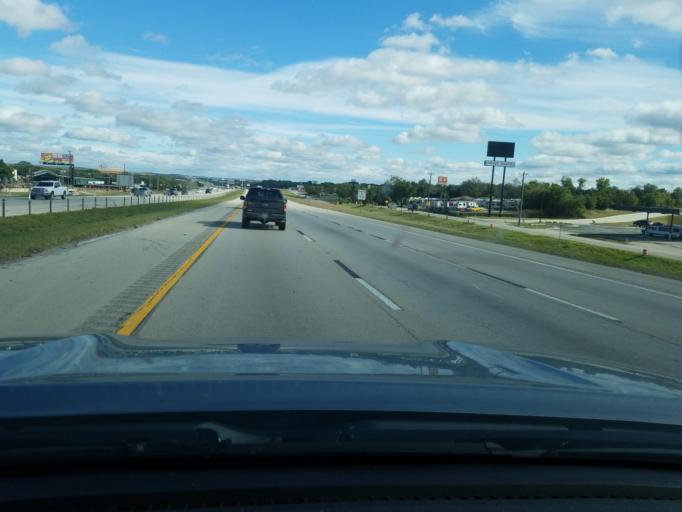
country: US
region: Texas
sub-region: Parker County
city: Hudson Oaks
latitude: 32.7493
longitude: -97.6785
